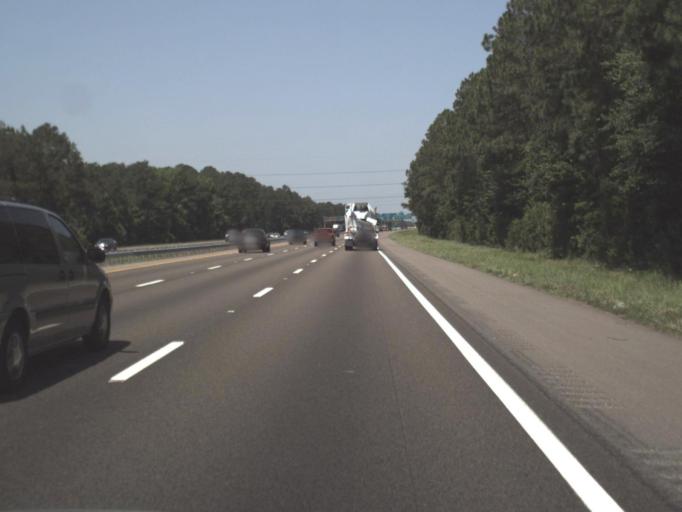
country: US
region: Florida
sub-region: Duval County
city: Baldwin
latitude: 30.3111
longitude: -81.8282
